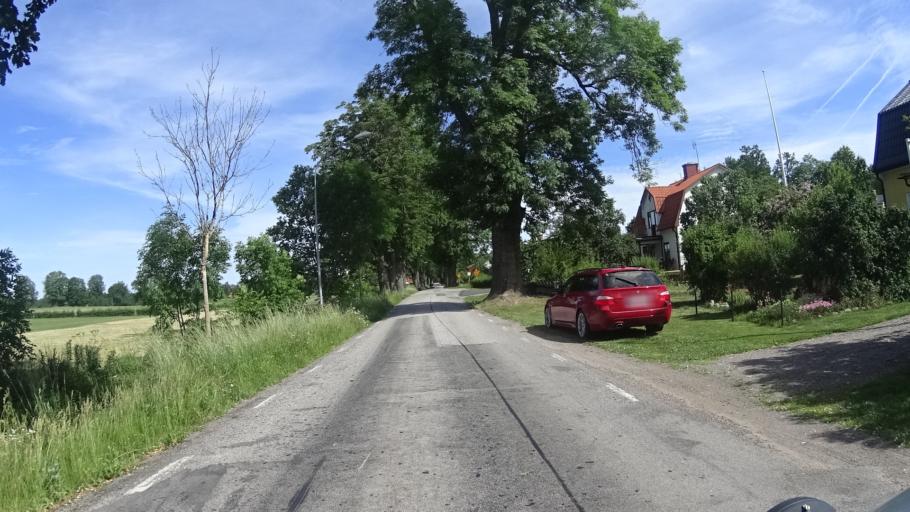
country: SE
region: Kalmar
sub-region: Vasterviks Kommun
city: Overum
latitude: 57.8918
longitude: 16.1701
